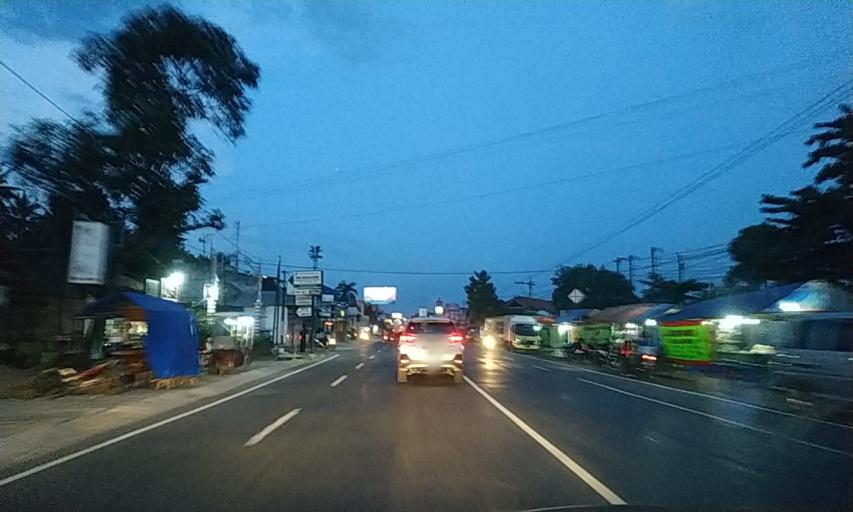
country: ID
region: Daerah Istimewa Yogyakarta
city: Godean
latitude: -7.8126
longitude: 110.2681
